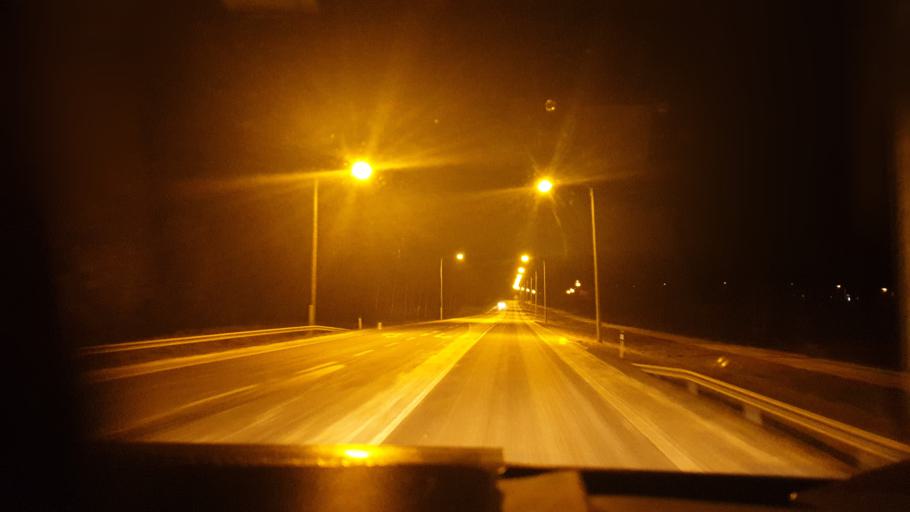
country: FI
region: Southern Ostrobothnia
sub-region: Kuusiokunnat
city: Alavus
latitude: 62.5960
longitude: 23.6397
